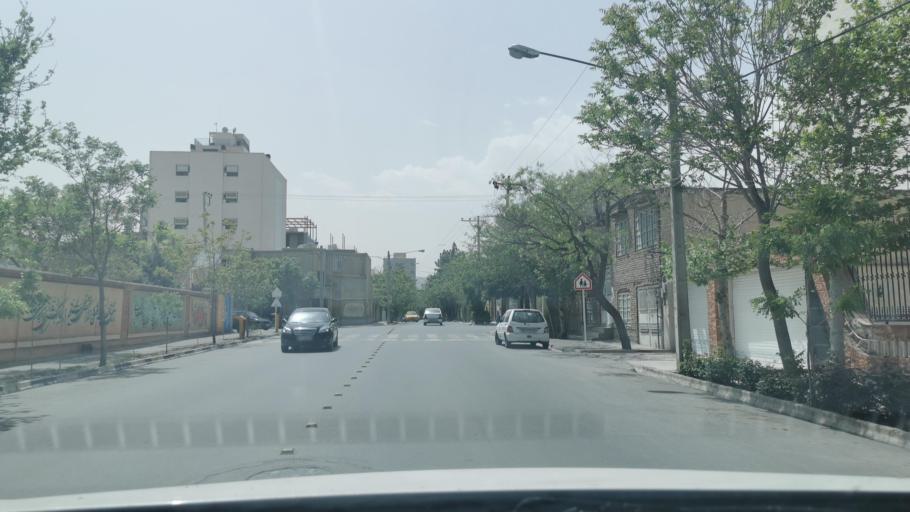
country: IR
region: Razavi Khorasan
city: Mashhad
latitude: 36.3360
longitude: 59.4814
